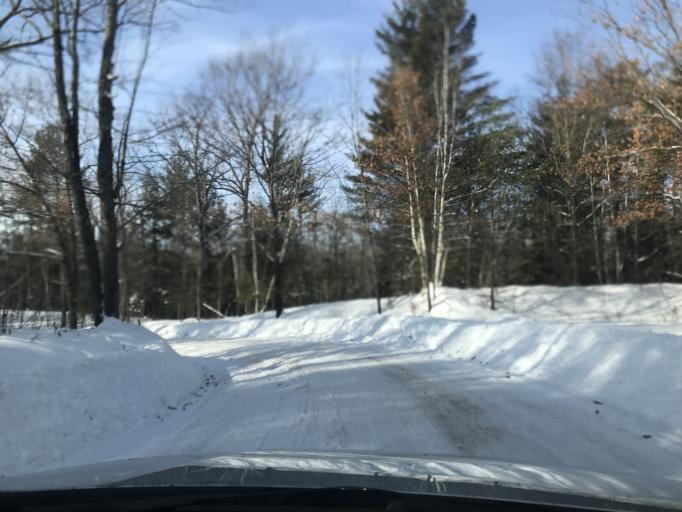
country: US
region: Wisconsin
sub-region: Oconto County
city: Gillett
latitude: 45.1498
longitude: -88.2381
